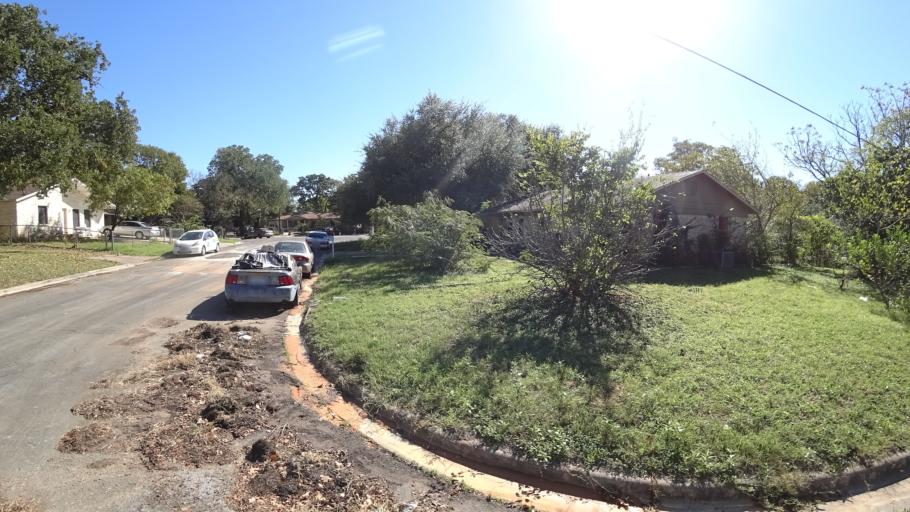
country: US
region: Texas
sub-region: Travis County
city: Austin
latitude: 30.2815
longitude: -97.6882
